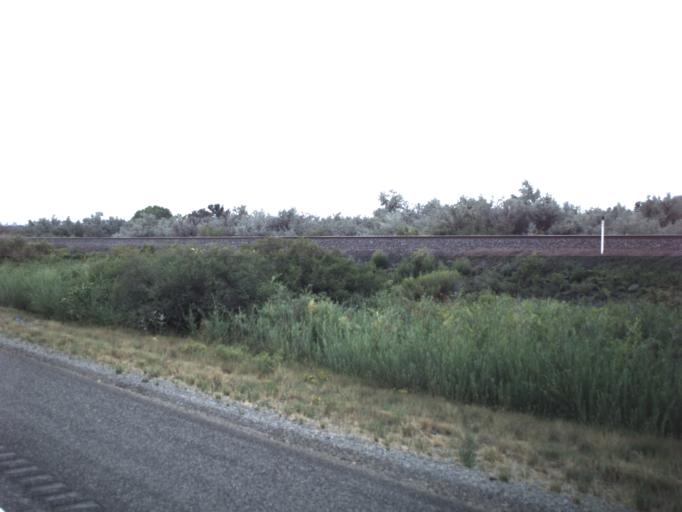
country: US
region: Utah
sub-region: Carbon County
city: Wellington
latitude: 39.5535
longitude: -110.7573
